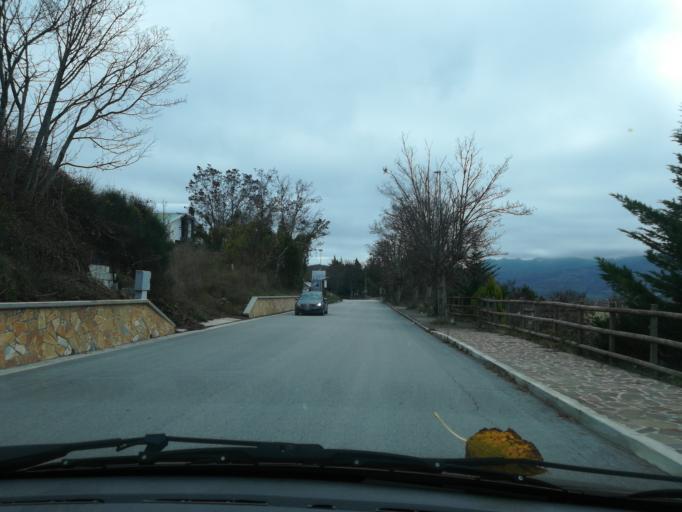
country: IT
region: Molise
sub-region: Provincia di Isernia
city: Agnone
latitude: 41.8168
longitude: 14.3726
